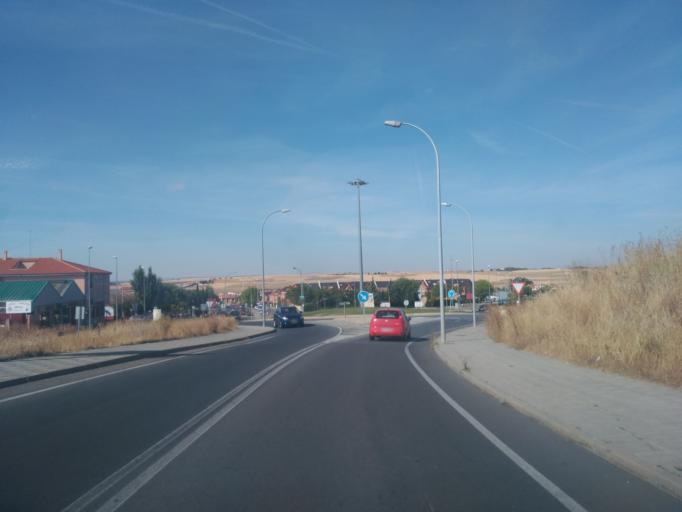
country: ES
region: Castille and Leon
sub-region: Provincia de Salamanca
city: Villamayor
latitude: 40.9945
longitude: -5.6923
